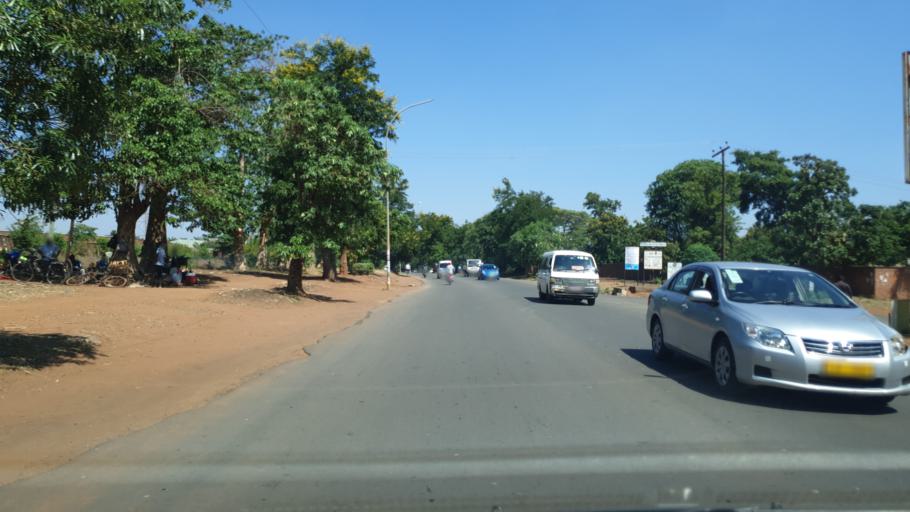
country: MW
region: Central Region
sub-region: Lilongwe District
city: Lilongwe
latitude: -13.9785
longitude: 33.7610
